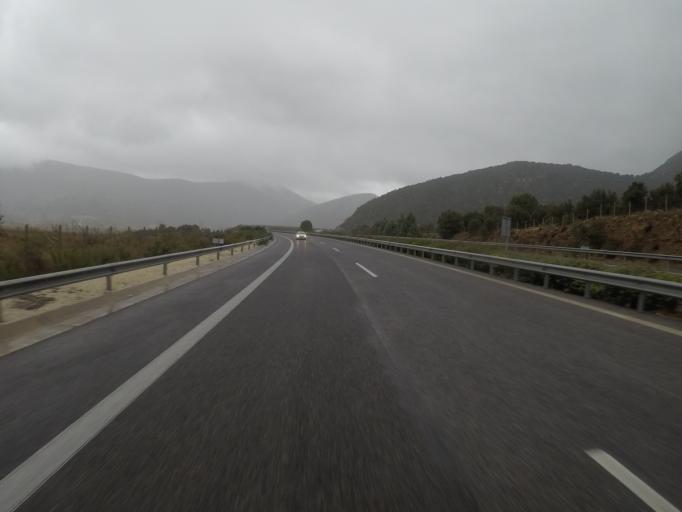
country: GR
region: Peloponnese
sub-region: Nomos Arkadias
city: Tripoli
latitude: 37.6334
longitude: 22.4666
